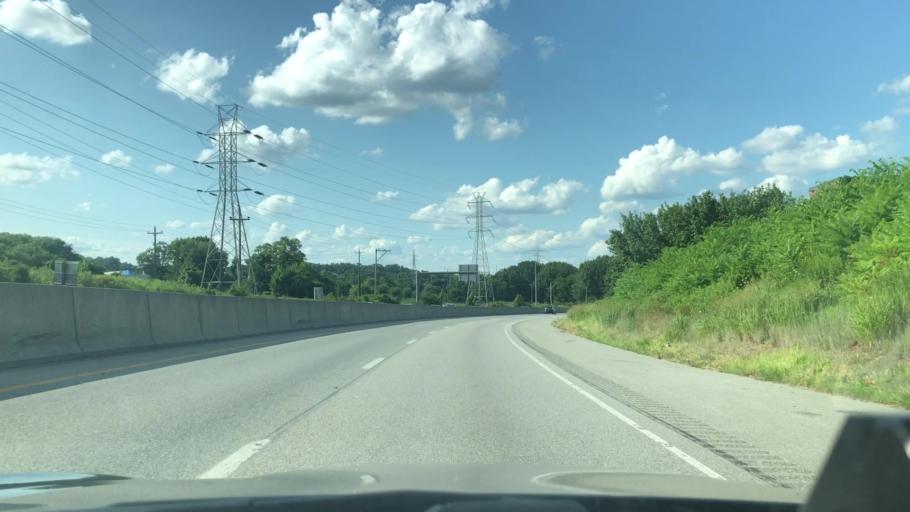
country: US
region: Pennsylvania
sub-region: Montgomery County
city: Flourtown
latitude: 40.1212
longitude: -75.2046
